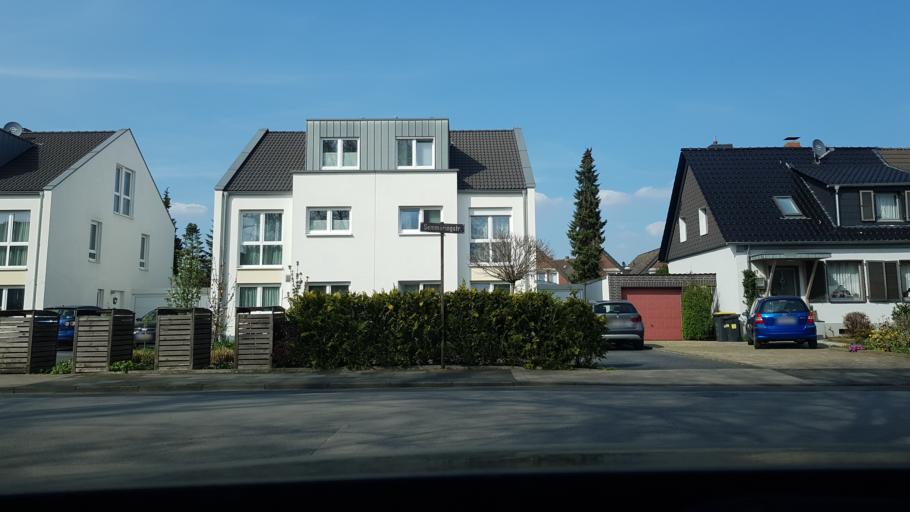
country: DE
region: North Rhine-Westphalia
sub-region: Regierungsbezirk Dusseldorf
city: Hochfeld
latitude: 51.3845
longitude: 6.7792
